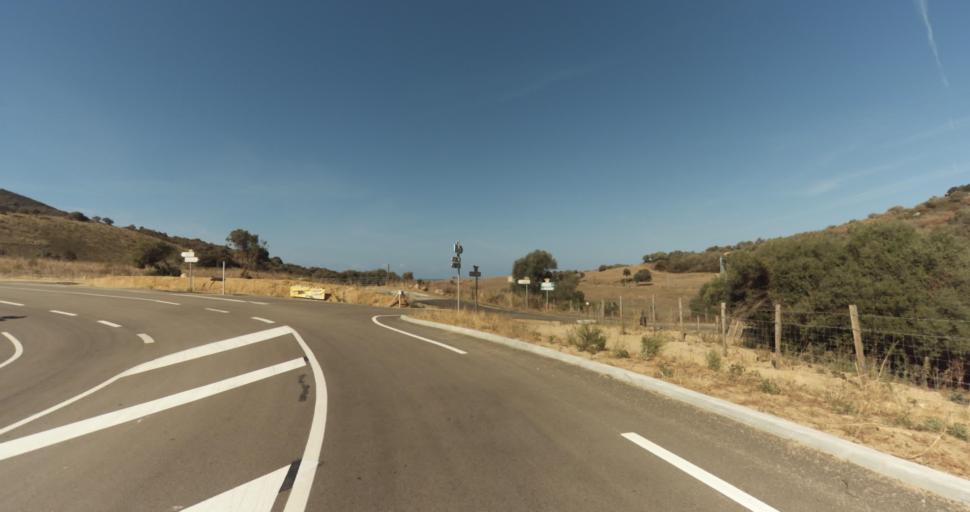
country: FR
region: Corsica
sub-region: Departement de la Corse-du-Sud
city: Ajaccio
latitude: 41.9301
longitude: 8.6485
